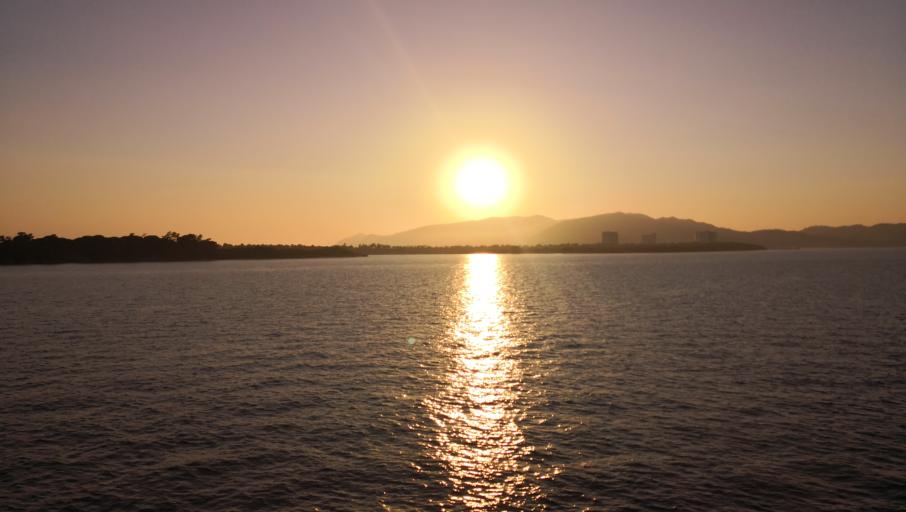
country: PT
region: Setubal
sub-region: Setubal
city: Setubal
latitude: 38.4897
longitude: -8.8757
